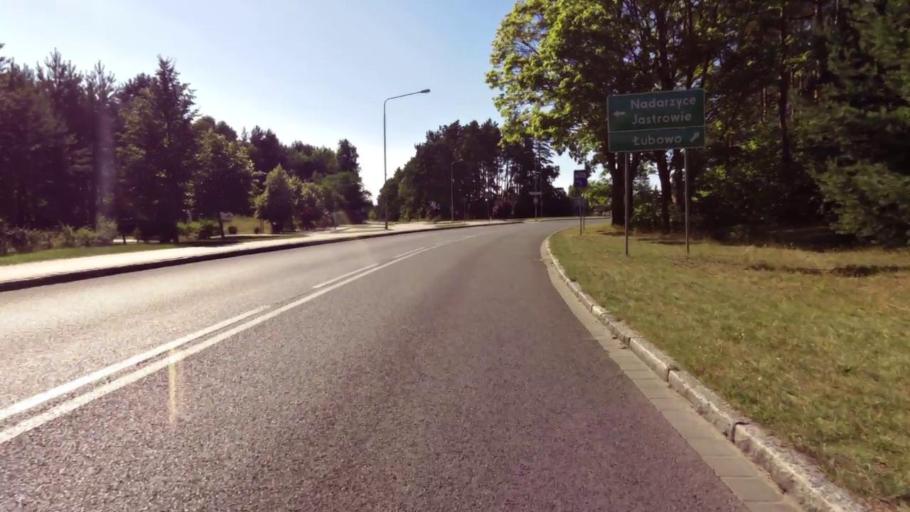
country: PL
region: West Pomeranian Voivodeship
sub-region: Powiat szczecinecki
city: Borne Sulinowo
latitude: 53.5757
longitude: 16.5532
